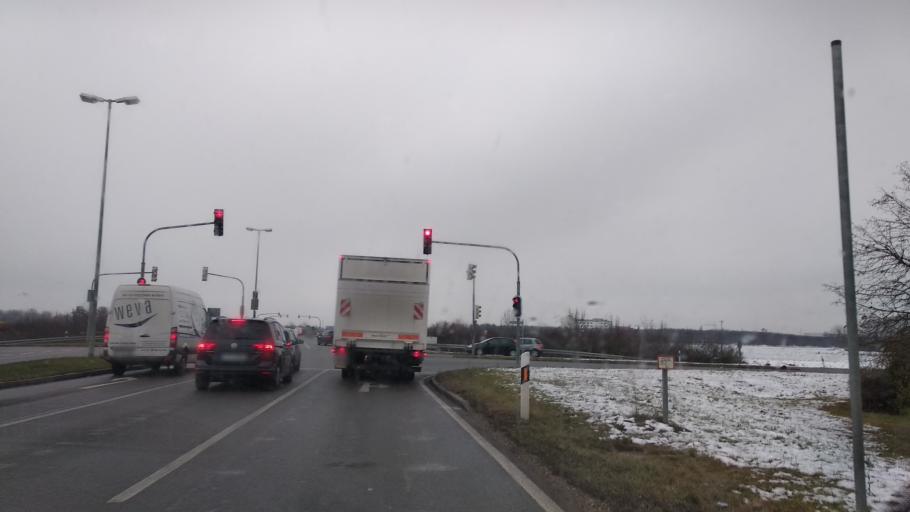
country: DE
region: Bavaria
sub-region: Upper Bavaria
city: Feldkirchen
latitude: 48.1466
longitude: 11.7458
